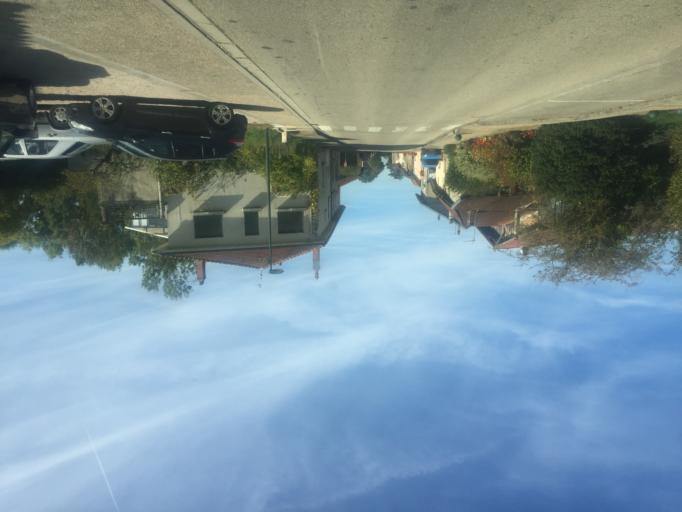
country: FR
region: Rhone-Alpes
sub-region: Departement de l'Ain
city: Marboz
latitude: 46.4098
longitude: 5.2622
